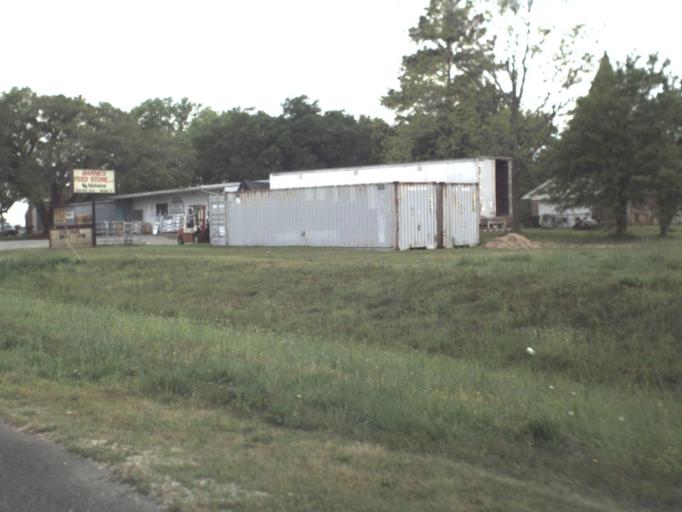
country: US
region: Florida
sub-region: Escambia County
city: Molino
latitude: 30.7032
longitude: -87.3505
